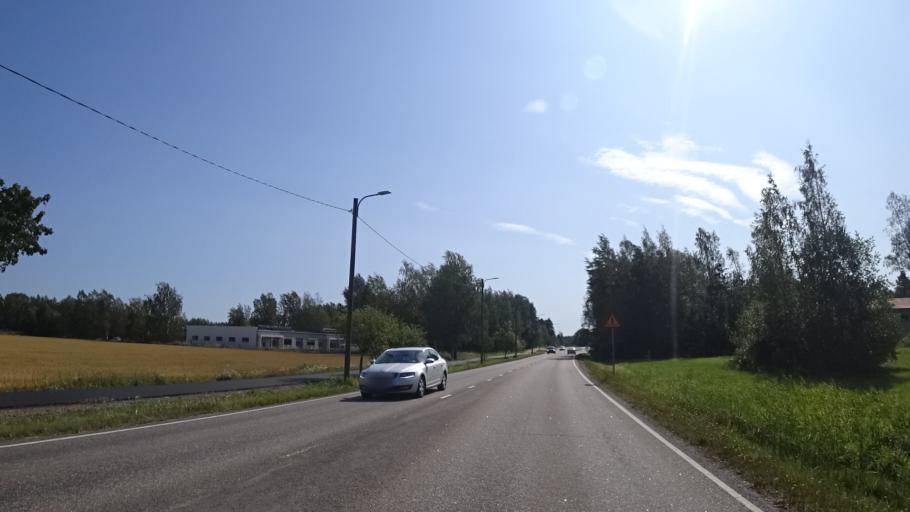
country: FI
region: Kymenlaakso
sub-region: Kotka-Hamina
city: Karhula
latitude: 60.5190
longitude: 26.9537
